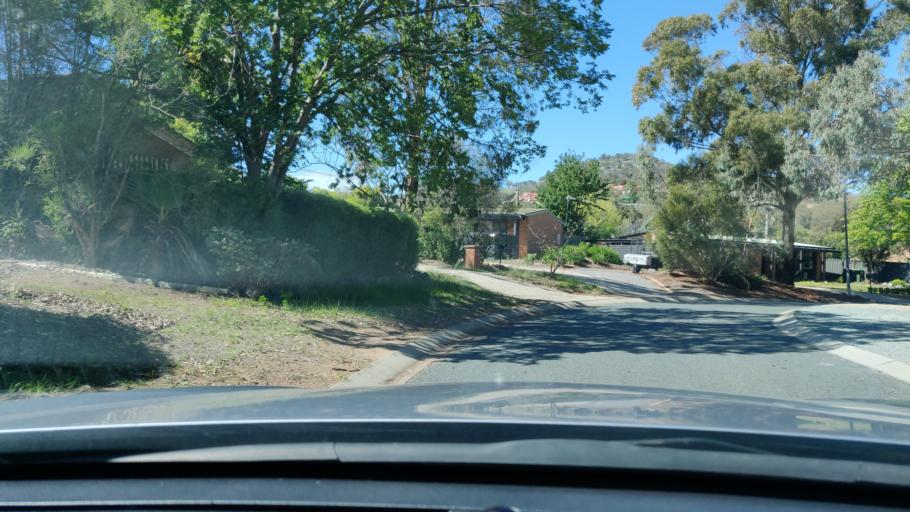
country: AU
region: Australian Capital Territory
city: Macarthur
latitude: -35.4413
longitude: 149.0972
